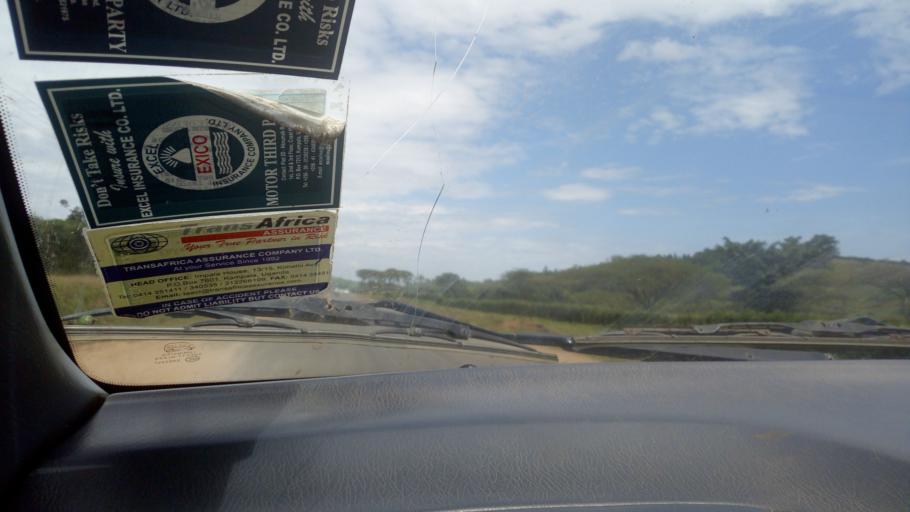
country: UG
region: Western Region
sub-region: Mbarara District
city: Bwizibwera
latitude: -0.3826
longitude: 30.5652
